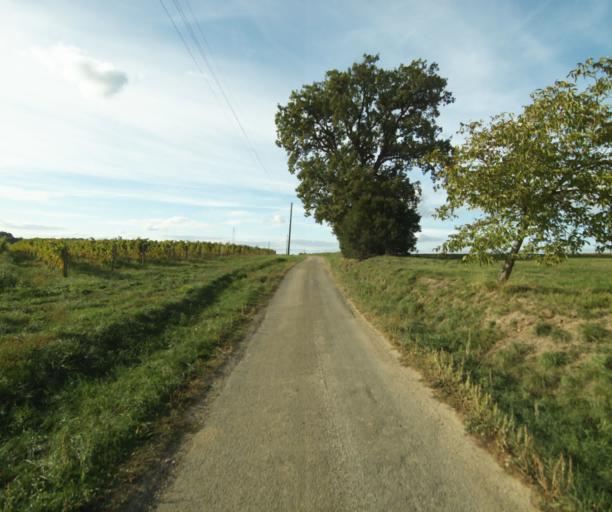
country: FR
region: Midi-Pyrenees
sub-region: Departement du Gers
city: Gondrin
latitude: 43.8967
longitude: 0.2636
